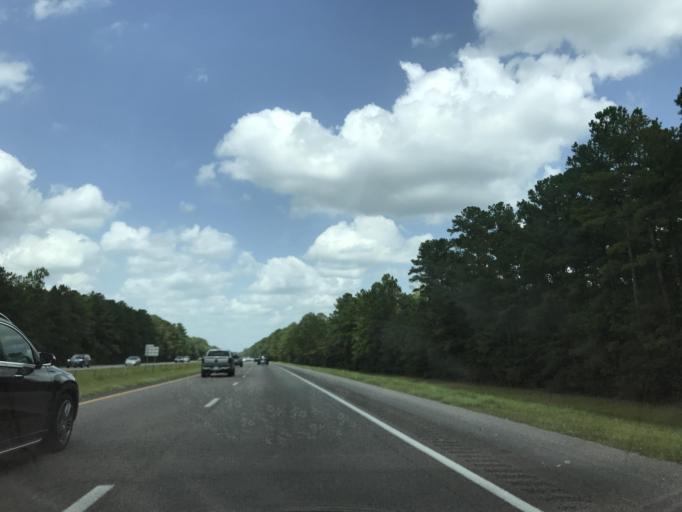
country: US
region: North Carolina
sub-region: Pender County
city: Burgaw
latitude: 34.5883
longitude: -77.9061
